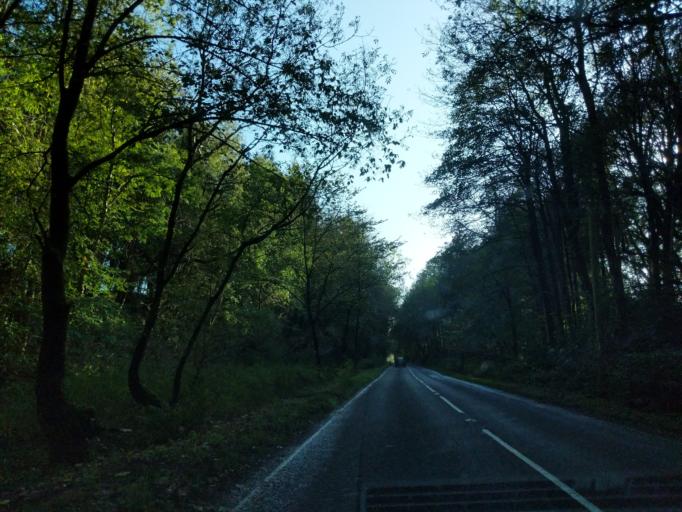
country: GB
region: Scotland
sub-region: Dumfries and Galloway
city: Kirkcudbright
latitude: 54.8988
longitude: -4.0118
